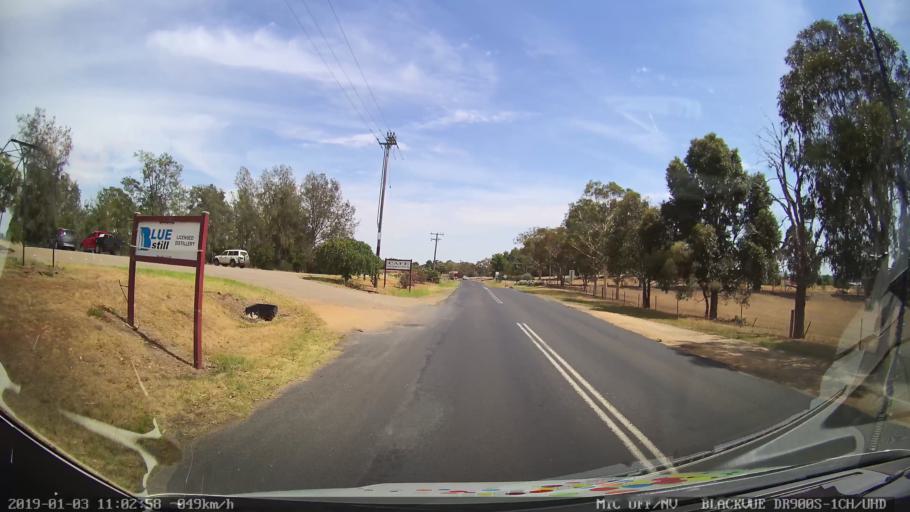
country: AU
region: New South Wales
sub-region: Young
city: Young
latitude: -34.2944
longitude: 148.2970
